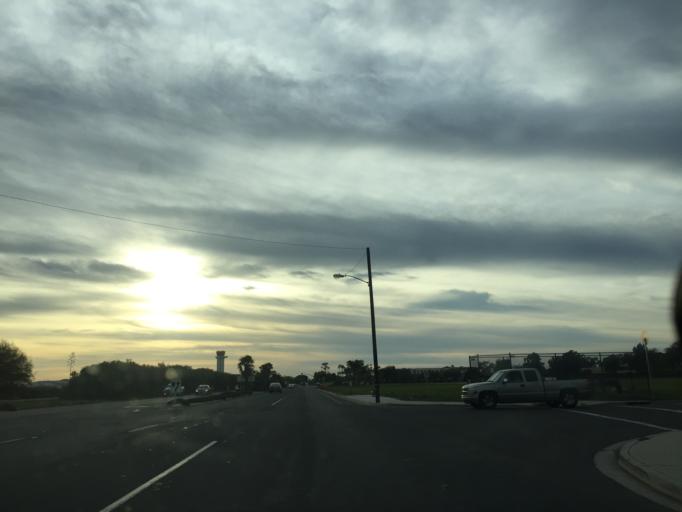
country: US
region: California
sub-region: Santa Barbara County
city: Goleta
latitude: 34.4337
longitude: -119.8382
